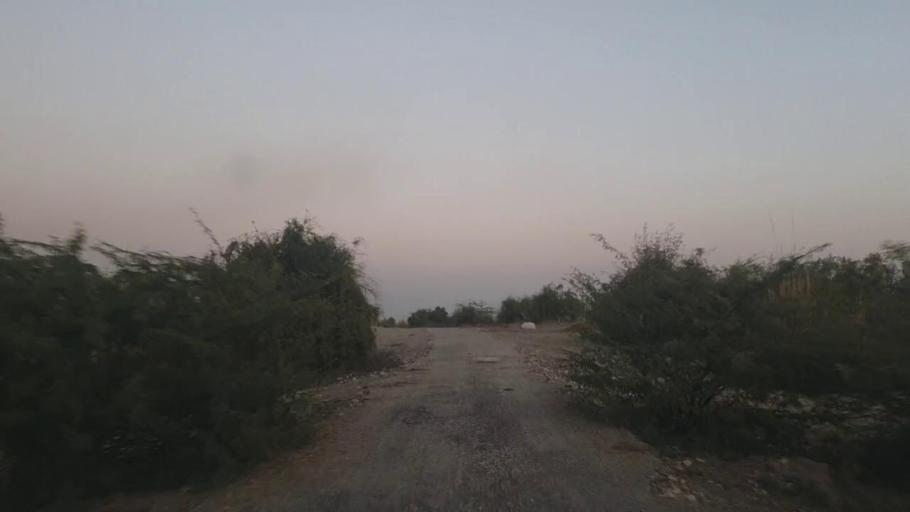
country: PK
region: Sindh
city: Jam Sahib
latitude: 26.3863
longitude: 68.8142
